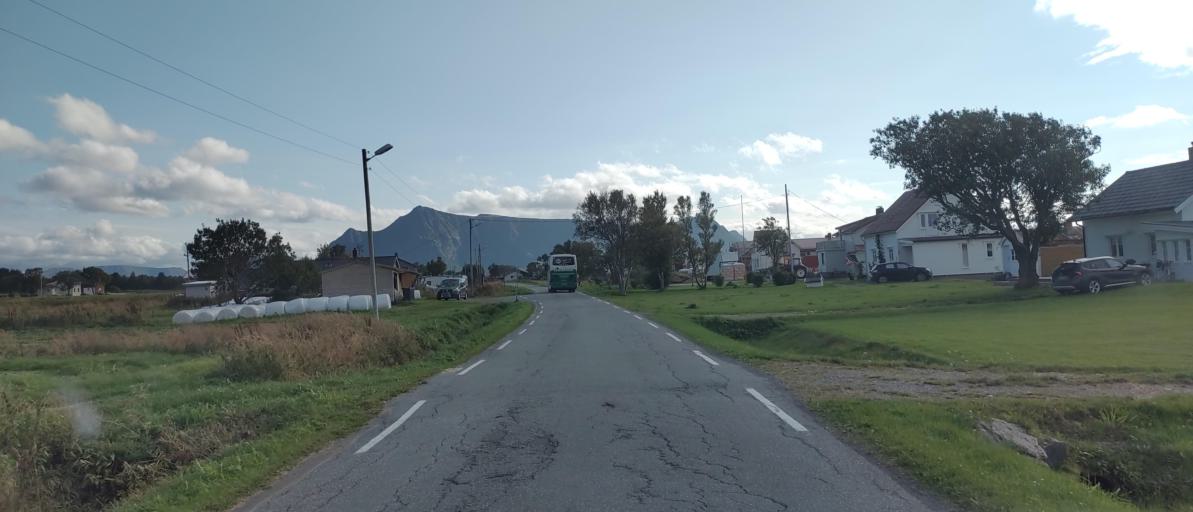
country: NO
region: Nordland
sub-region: Sortland
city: Sortland
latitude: 69.0455
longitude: 15.5156
